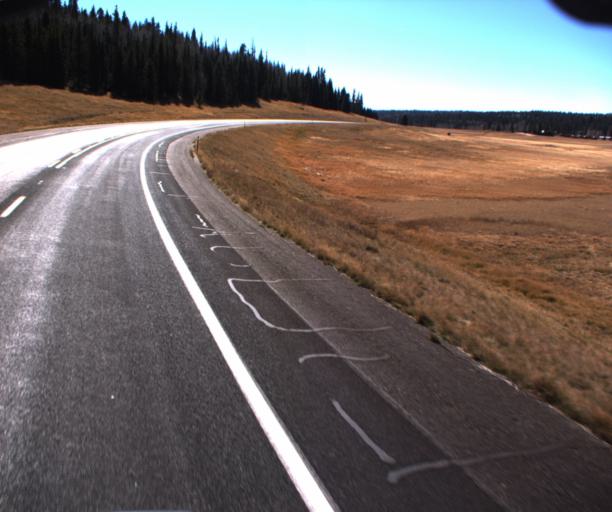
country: US
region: Arizona
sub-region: Coconino County
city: Grand Canyon
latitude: 36.4214
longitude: -112.1286
